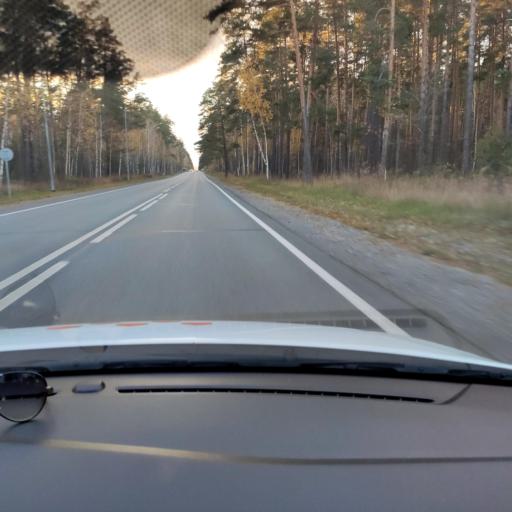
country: RU
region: Tatarstan
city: Stolbishchi
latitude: 55.6356
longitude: 49.0724
